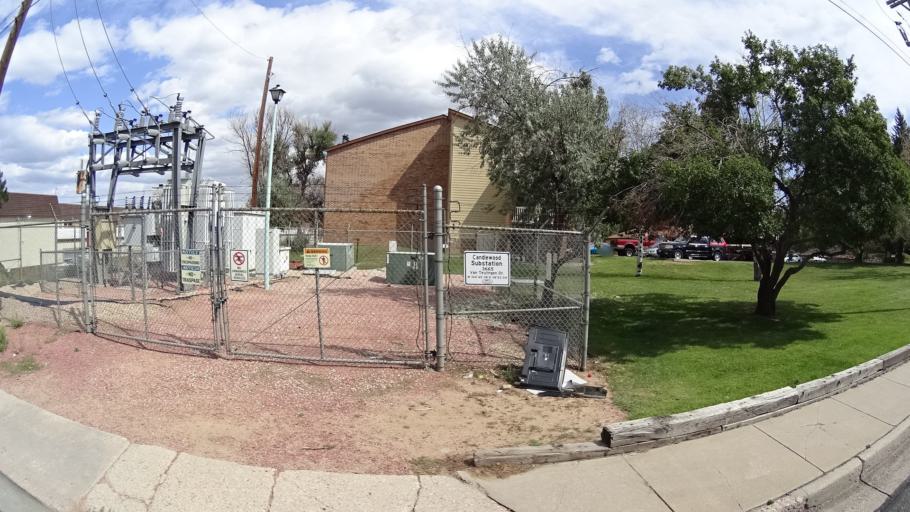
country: US
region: Colorado
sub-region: El Paso County
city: Cimarron Hills
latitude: 38.8844
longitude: -104.7608
